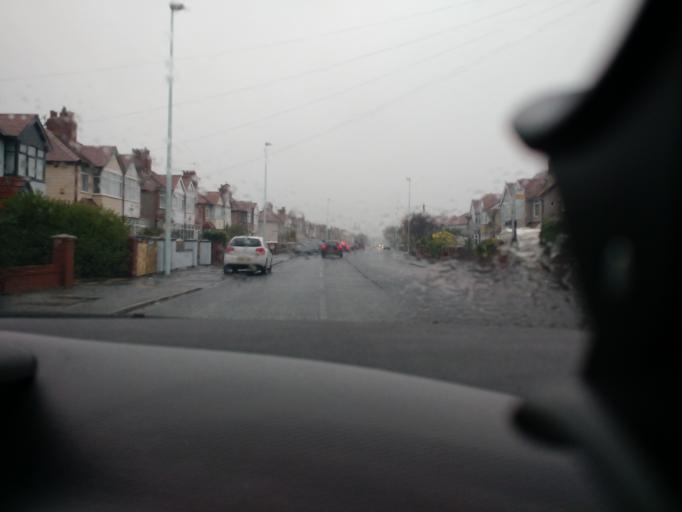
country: GB
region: England
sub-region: Lancashire
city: Cleveleys
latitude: 53.8726
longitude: -3.0332
